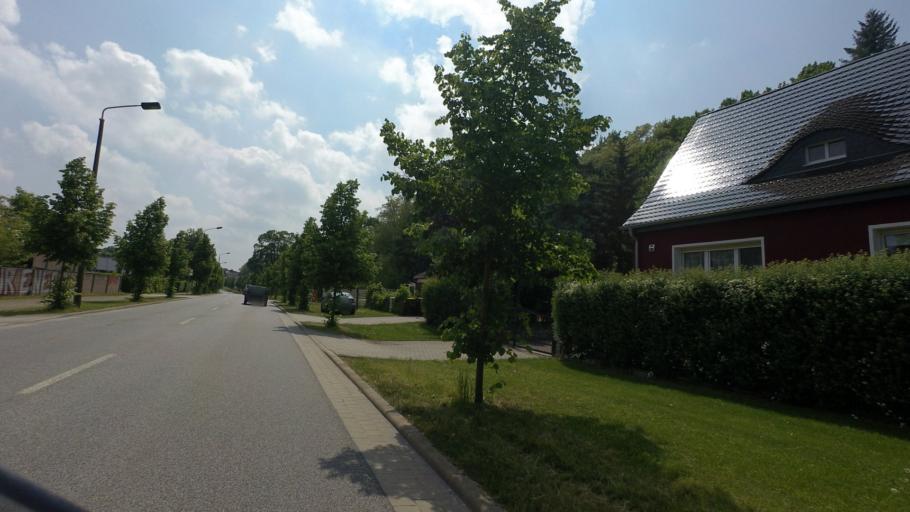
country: DE
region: Brandenburg
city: Spremberg
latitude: 51.5760
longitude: 14.3637
